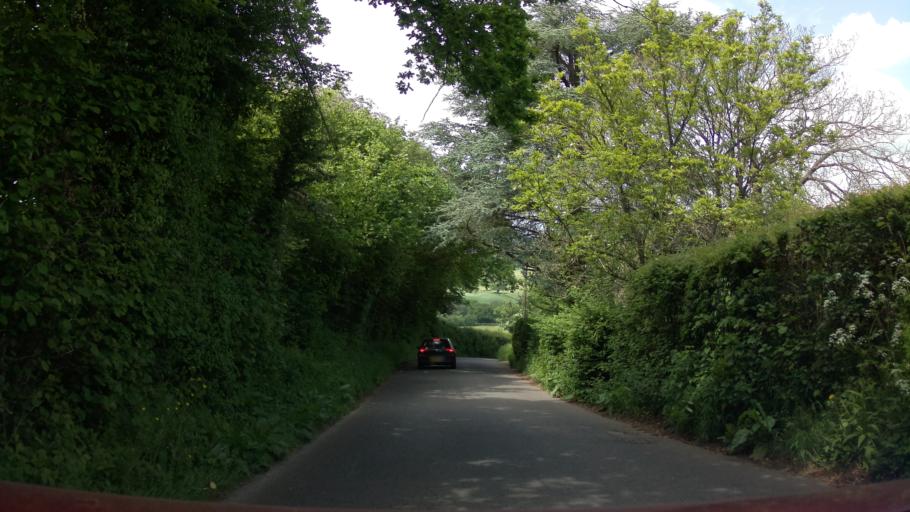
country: GB
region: England
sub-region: Herefordshire
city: Llanrothal
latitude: 51.8718
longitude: -2.8047
